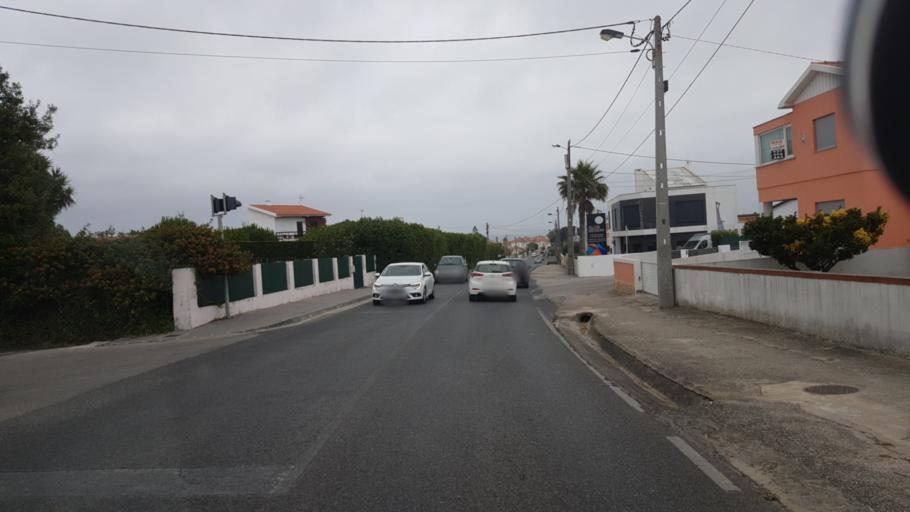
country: PT
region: Lisbon
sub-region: Torres Vedras
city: Silveira
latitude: 39.1186
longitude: -9.3732
